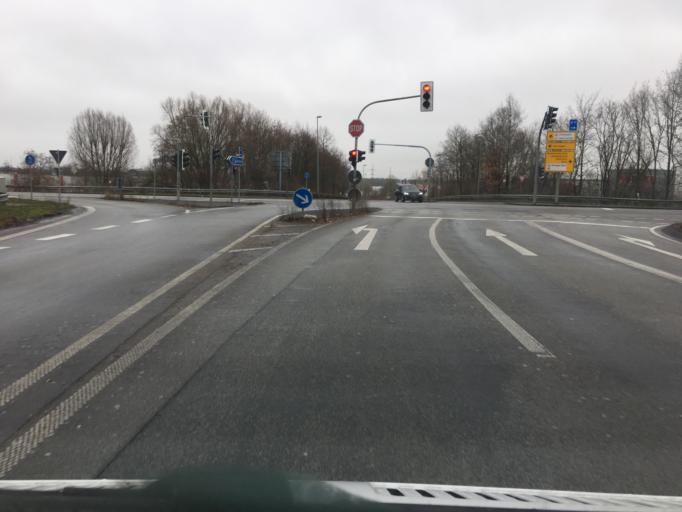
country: DE
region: North Rhine-Westphalia
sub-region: Regierungsbezirk Dusseldorf
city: Dormagen
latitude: 51.0951
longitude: 6.8068
